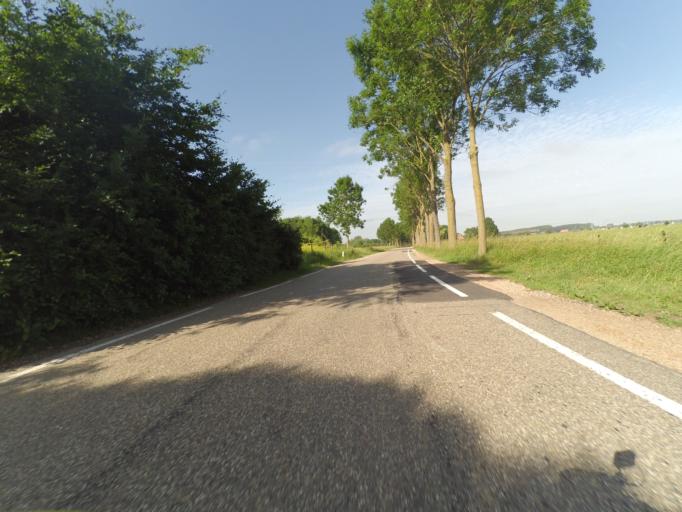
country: NL
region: Gelderland
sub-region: Gemeente Culemborg
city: Culemborg
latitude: 51.9391
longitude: 5.2785
